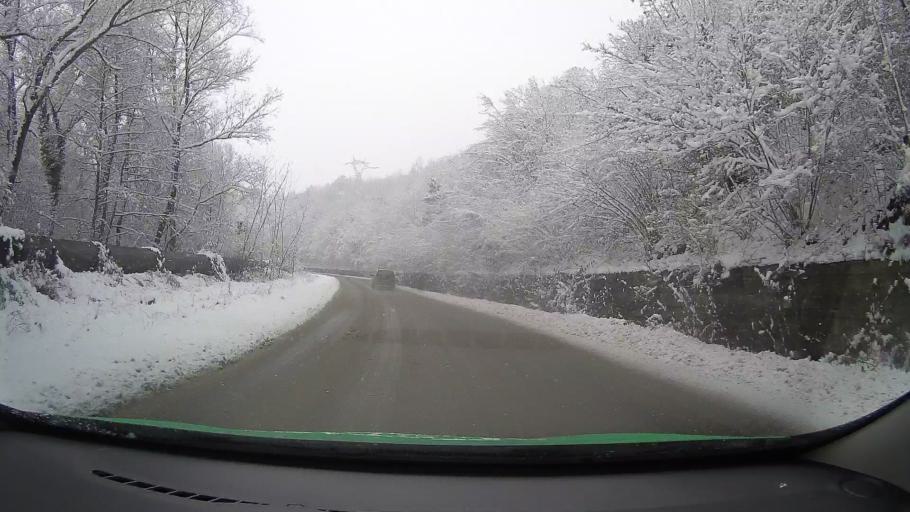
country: RO
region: Hunedoara
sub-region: Comuna Teliucu Inferior
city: Teliucu Inferior
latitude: 45.7269
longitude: 22.8790
